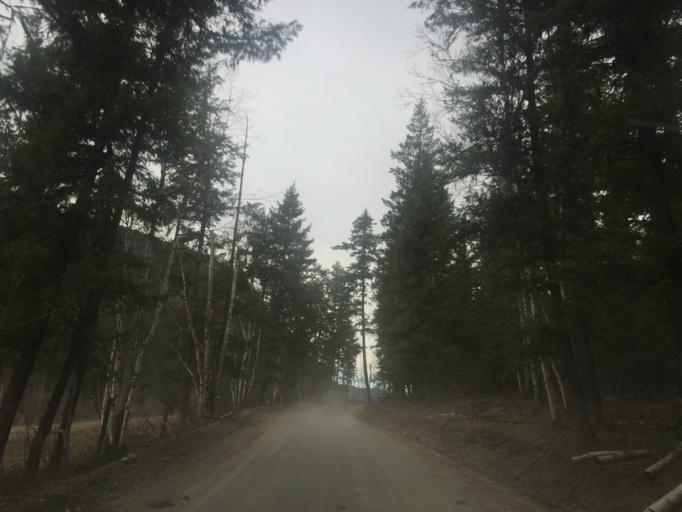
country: CA
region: British Columbia
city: Chase
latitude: 51.3912
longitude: -120.1264
